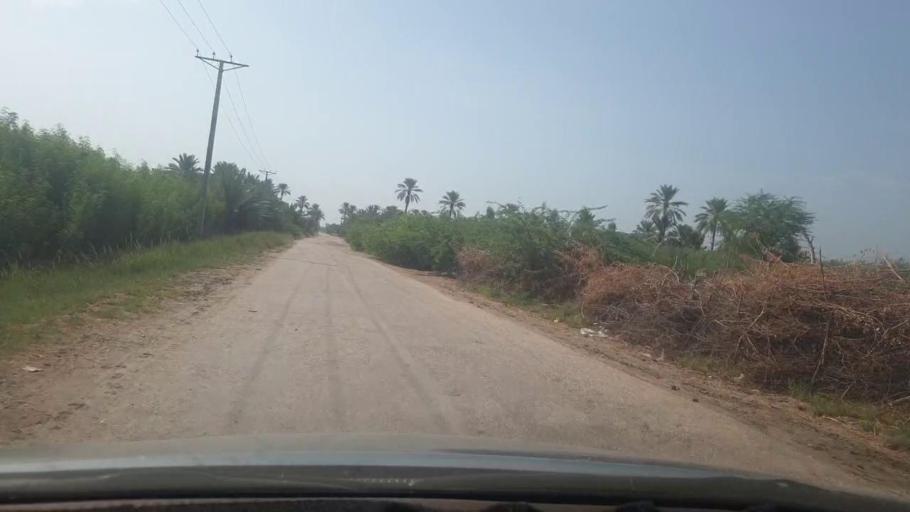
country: PK
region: Sindh
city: Gambat
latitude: 27.3276
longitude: 68.5513
